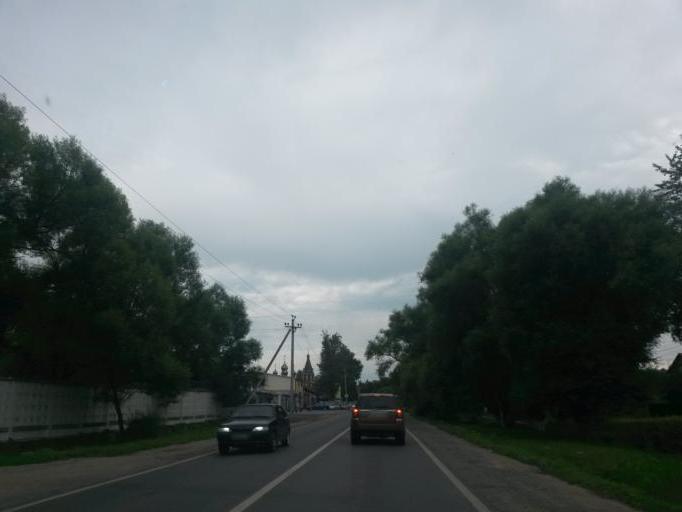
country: RU
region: Moskovskaya
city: Vostryakovo
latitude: 55.3977
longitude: 37.8101
